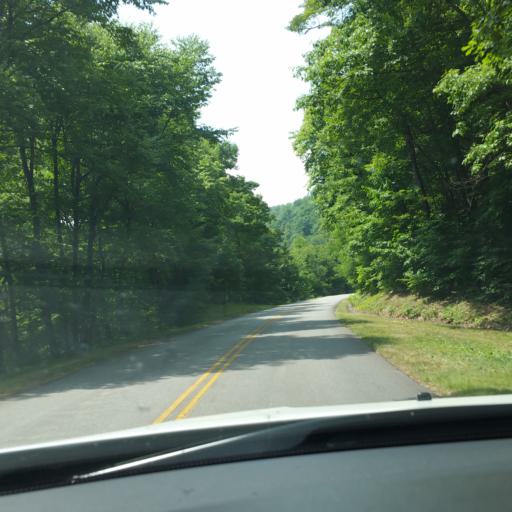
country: US
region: North Carolina
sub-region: Buncombe County
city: Avery Creek
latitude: 35.4529
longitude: -82.6403
